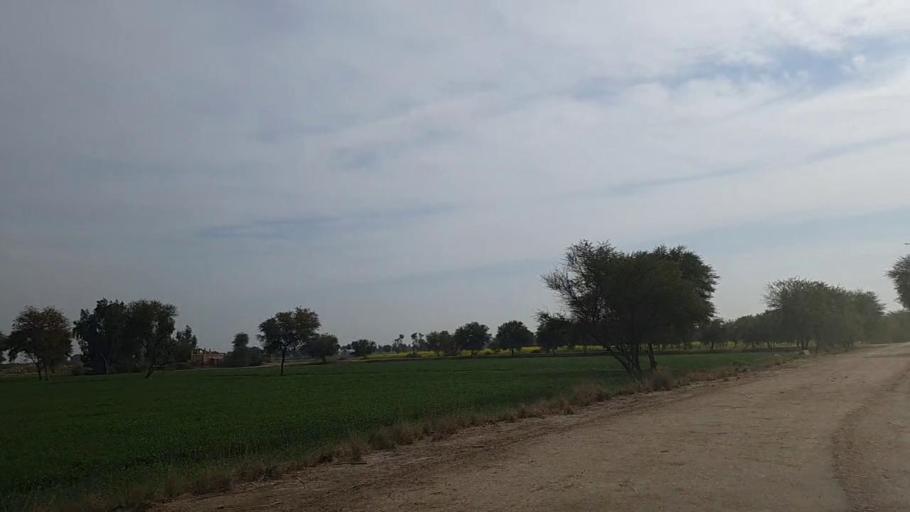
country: PK
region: Sindh
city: Daur
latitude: 26.4105
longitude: 68.4535
